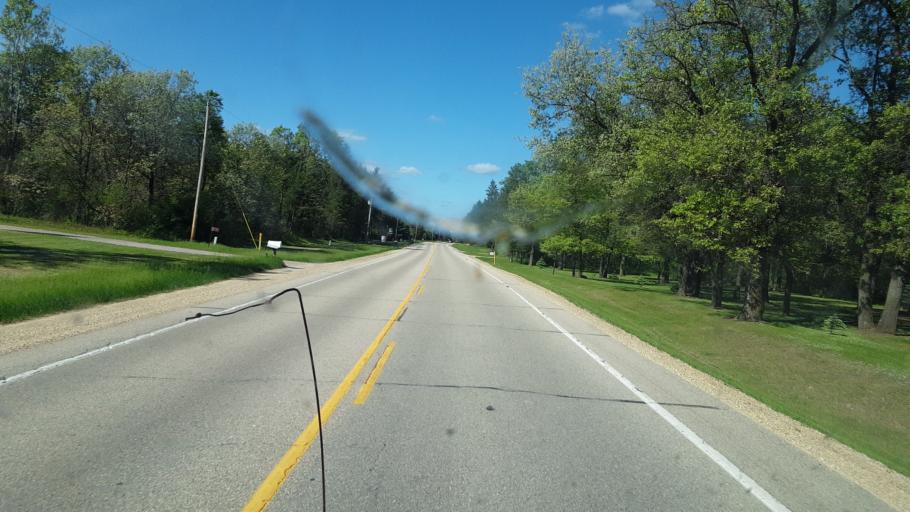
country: US
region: Wisconsin
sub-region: Juneau County
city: New Lisbon
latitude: 43.9248
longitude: -90.1108
